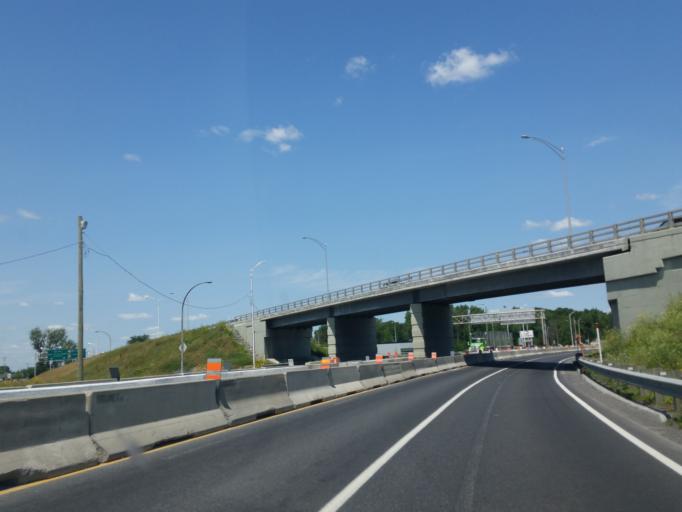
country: CA
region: Quebec
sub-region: Monteregie
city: Saint-Jean-sur-Richelieu
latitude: 45.3478
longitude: -73.2884
